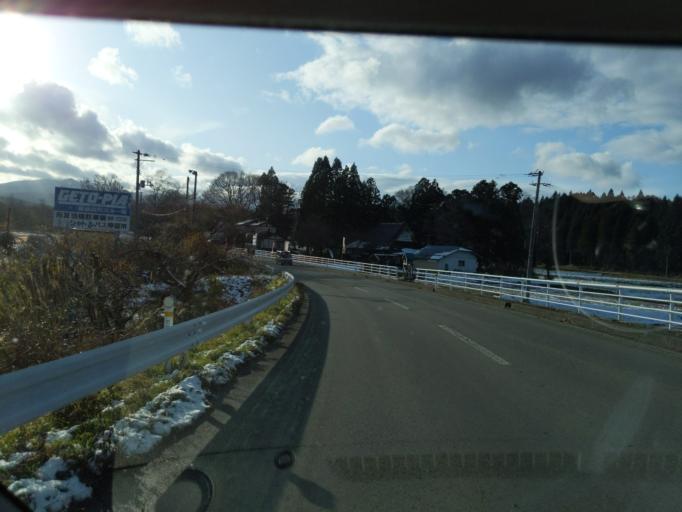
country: JP
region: Iwate
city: Kitakami
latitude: 39.2538
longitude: 141.0220
